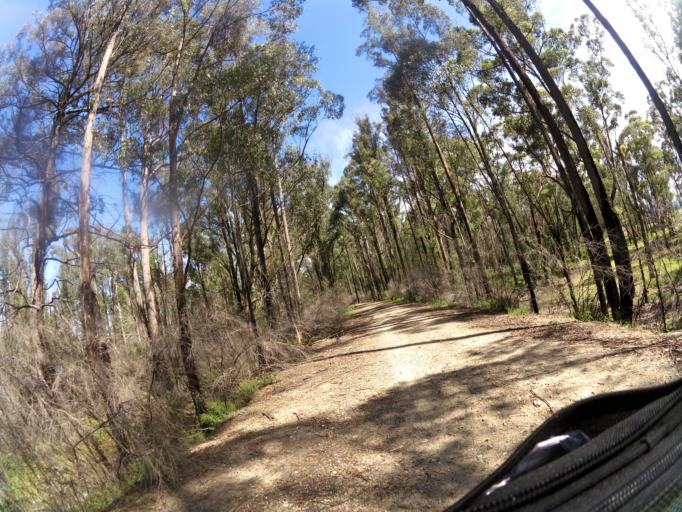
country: AU
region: Victoria
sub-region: East Gippsland
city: Lakes Entrance
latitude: -37.7269
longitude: 148.1606
